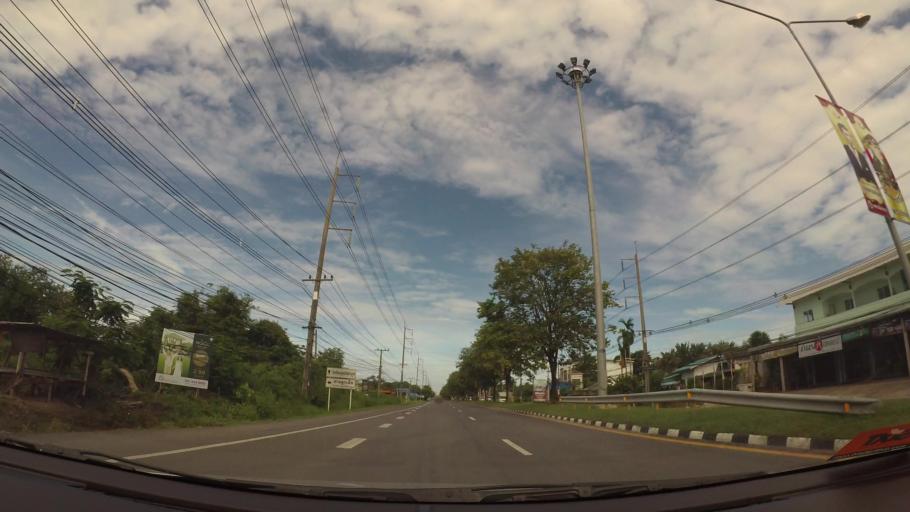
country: TH
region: Rayong
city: Ban Chang
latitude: 12.7415
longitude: 101.0891
